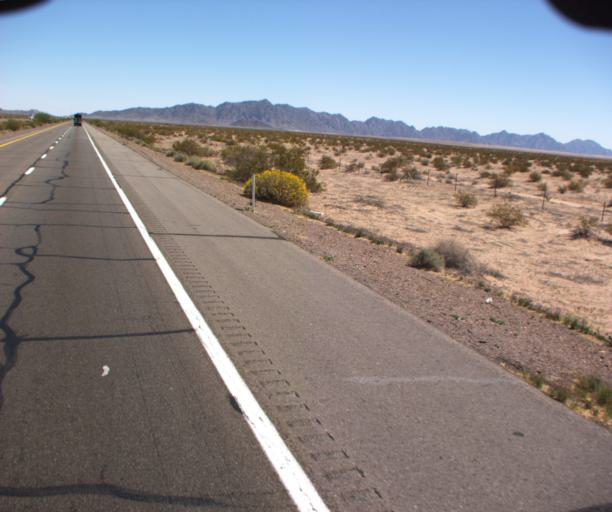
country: US
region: Arizona
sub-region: Yuma County
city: Wellton
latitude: 32.7095
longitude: -113.8475
